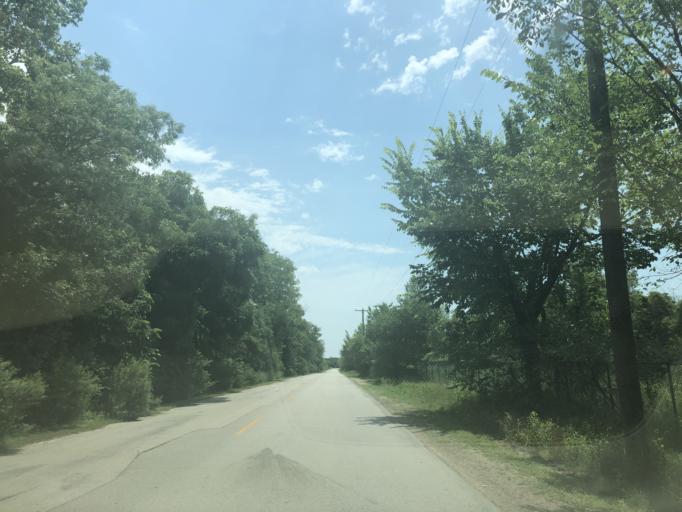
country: US
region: Texas
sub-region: Dallas County
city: Irving
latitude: 32.7866
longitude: -96.9408
